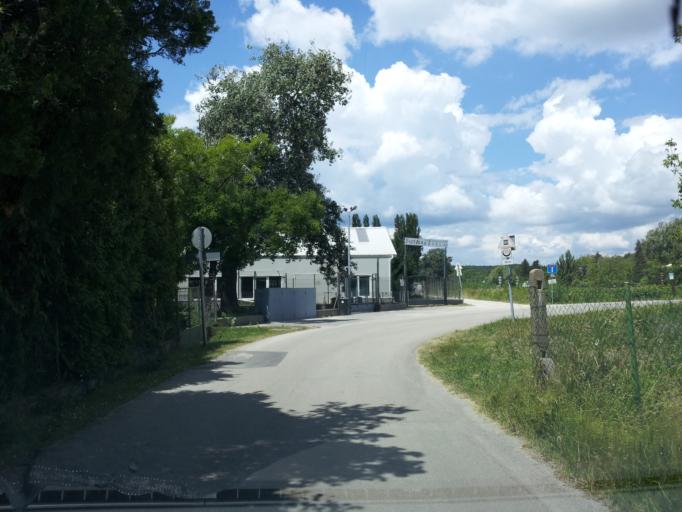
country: HU
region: Veszprem
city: Balatonkenese
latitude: 47.0331
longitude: 18.0943
